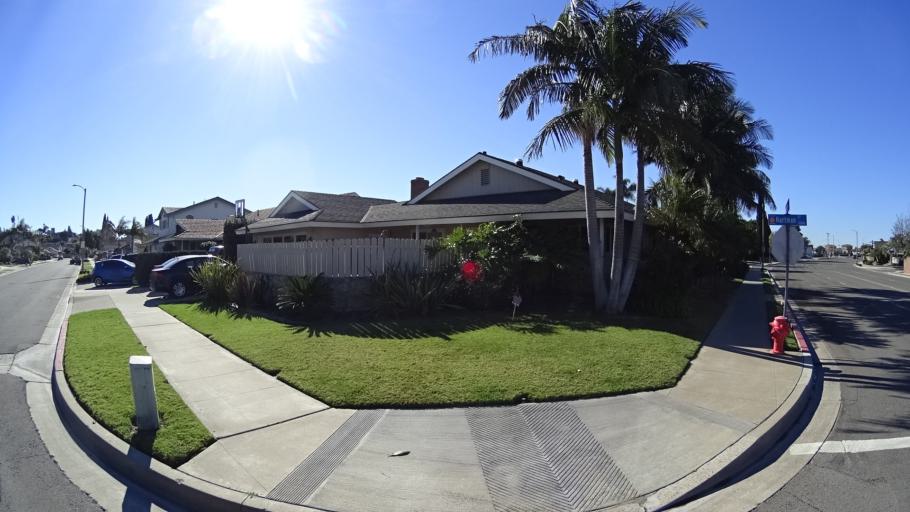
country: US
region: California
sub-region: Orange County
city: Placentia
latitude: 33.8433
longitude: -117.8501
